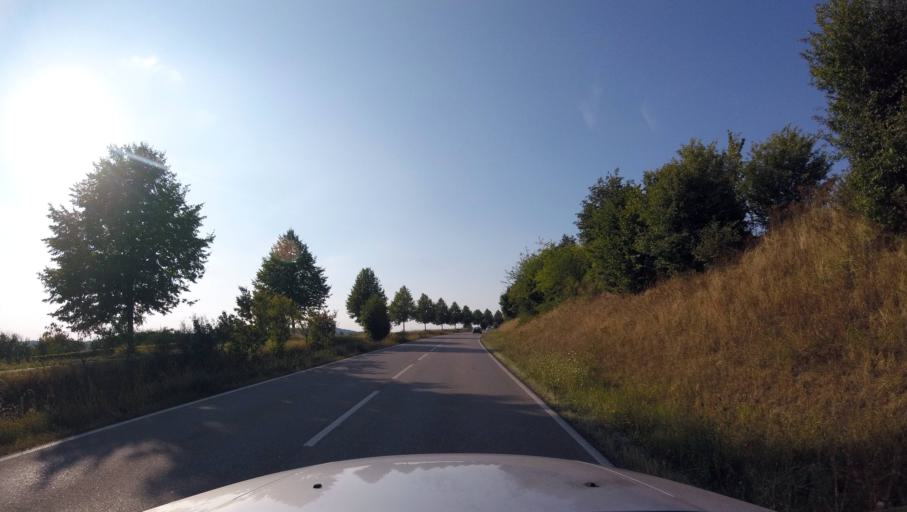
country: DE
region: Baden-Wuerttemberg
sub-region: Regierungsbezirk Stuttgart
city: Welzheim
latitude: 48.8665
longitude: 9.6256
